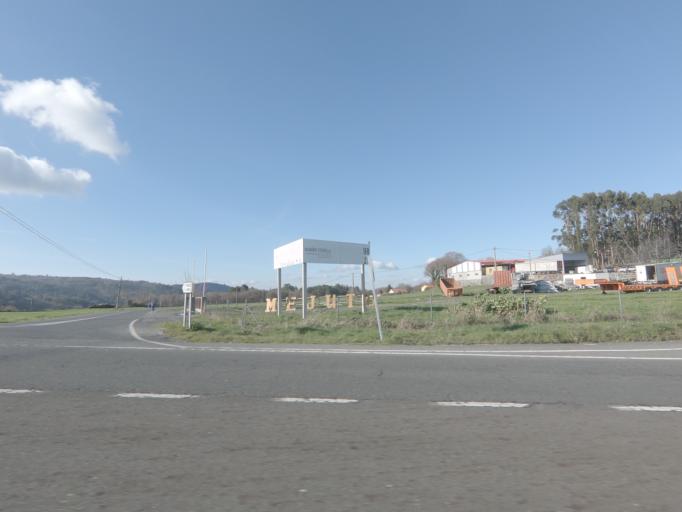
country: ES
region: Galicia
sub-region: Provincia de Pontevedra
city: Silleda
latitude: 42.6993
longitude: -8.3179
